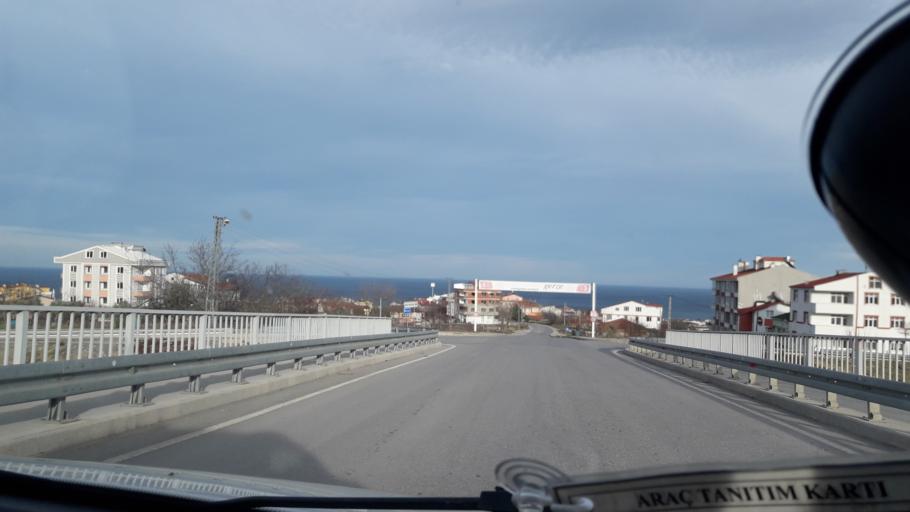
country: TR
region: Sinop
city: Gerze
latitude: 41.8016
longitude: 35.1781
